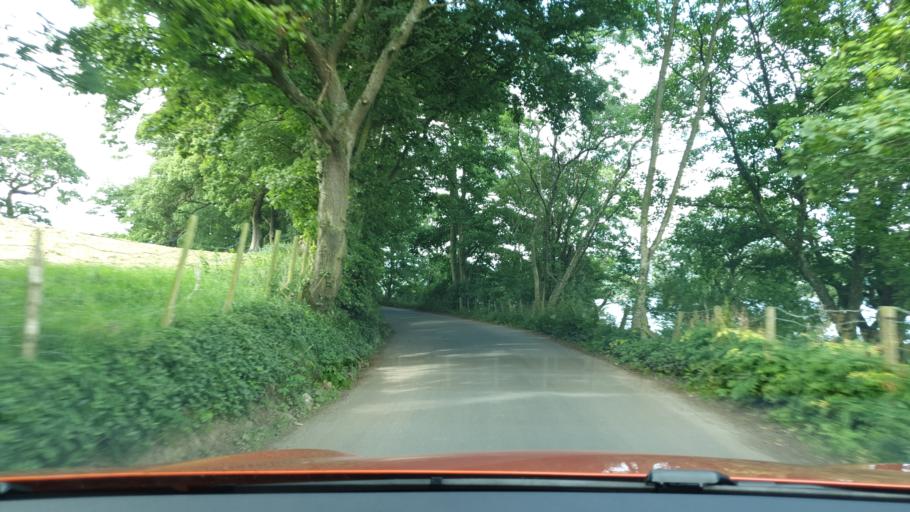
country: GB
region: England
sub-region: Cumbria
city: Penrith
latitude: 54.5988
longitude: -2.8345
